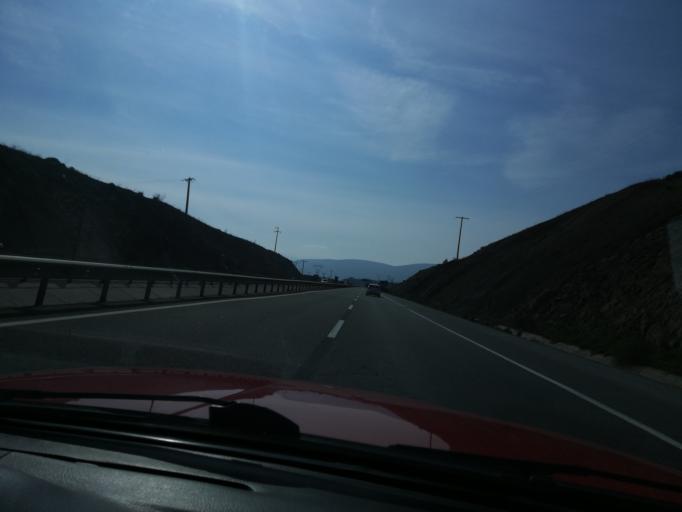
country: TR
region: Bilecik
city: Osmaneli
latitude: 40.3353
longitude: 30.0489
